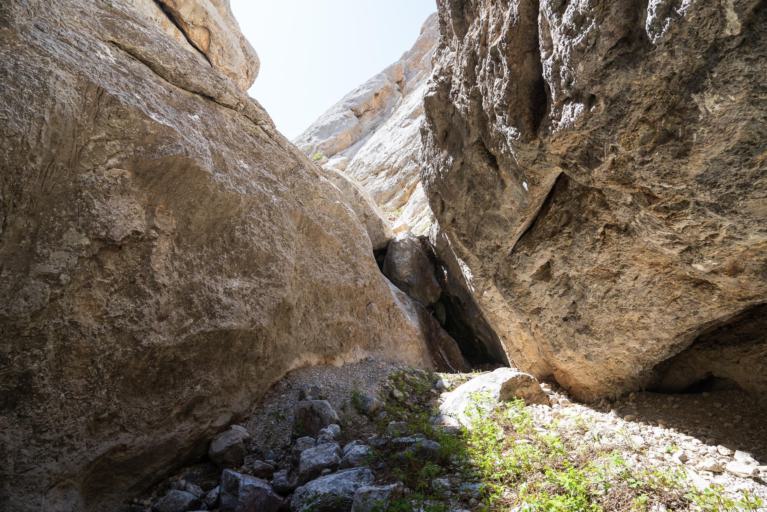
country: KZ
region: Ongtustik Qazaqstan
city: Ashchysay
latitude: 43.7679
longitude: 68.7949
